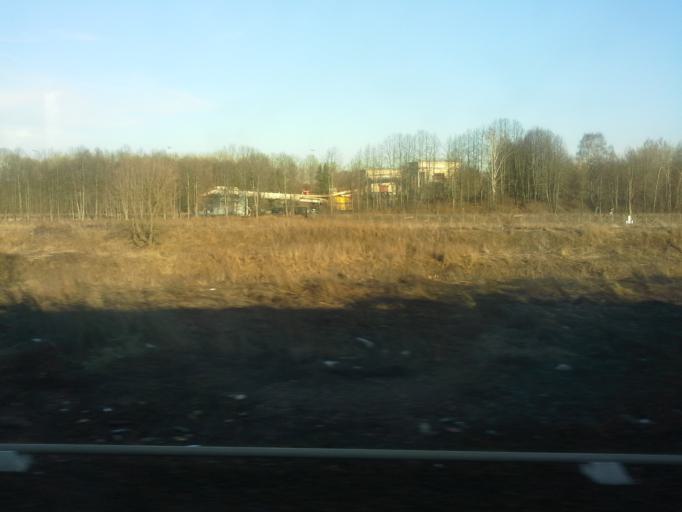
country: RU
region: Moskovskaya
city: Iksha
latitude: 56.1701
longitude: 37.5082
